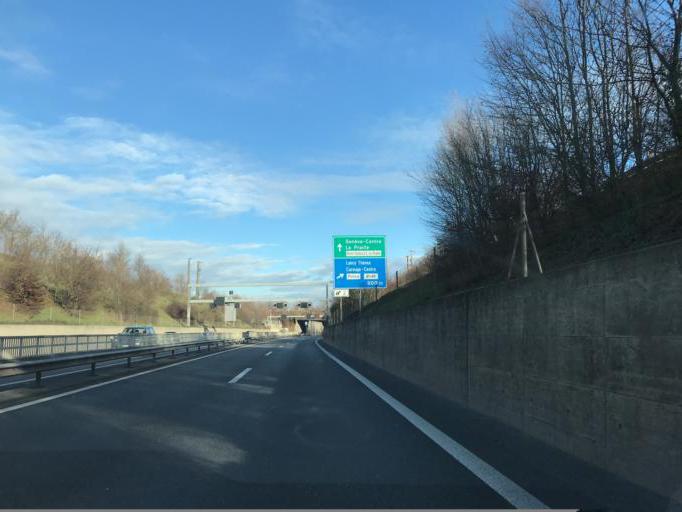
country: CH
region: Geneva
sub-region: Geneva
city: Plan-les-Ouates
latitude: 46.1621
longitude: 6.1184
